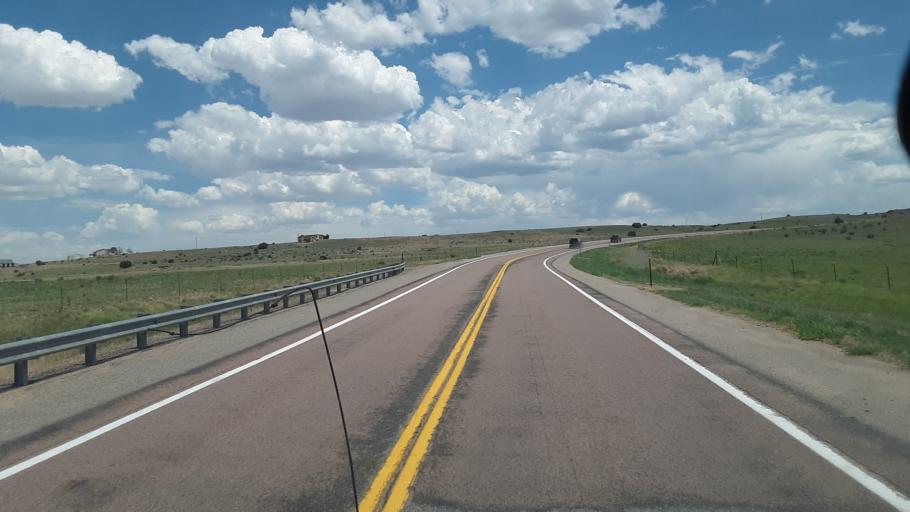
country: US
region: Colorado
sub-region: Fremont County
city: Florence
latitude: 38.2999
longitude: -105.0903
